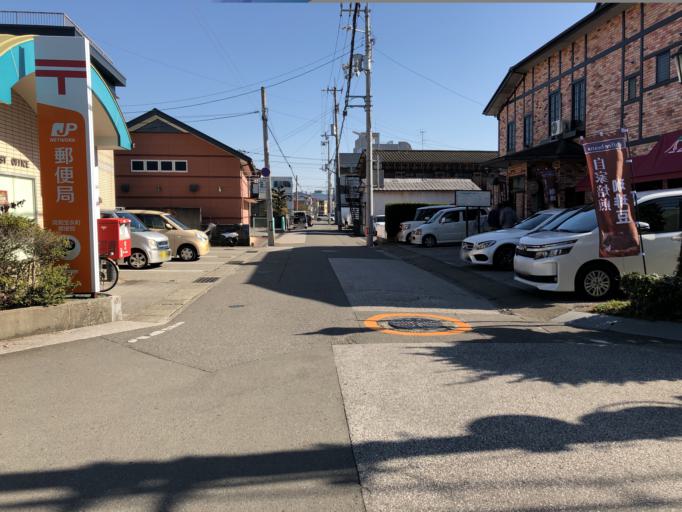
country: JP
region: Kochi
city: Kochi-shi
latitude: 33.5606
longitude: 133.5539
